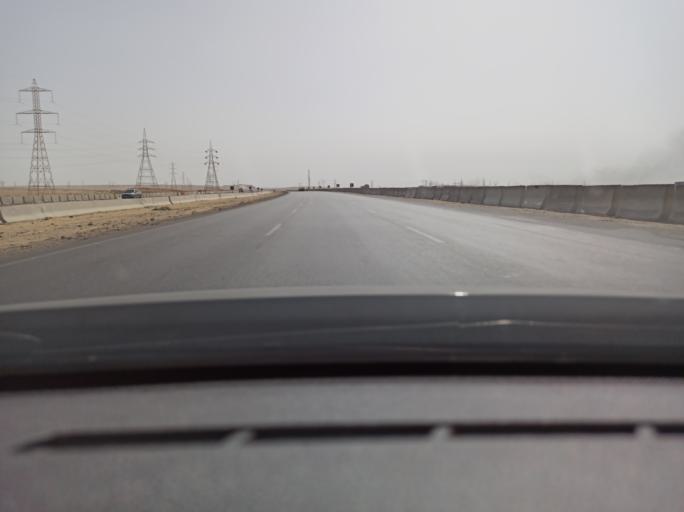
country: EG
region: Muhafazat al Qahirah
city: Halwan
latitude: 29.7684
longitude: 31.3827
